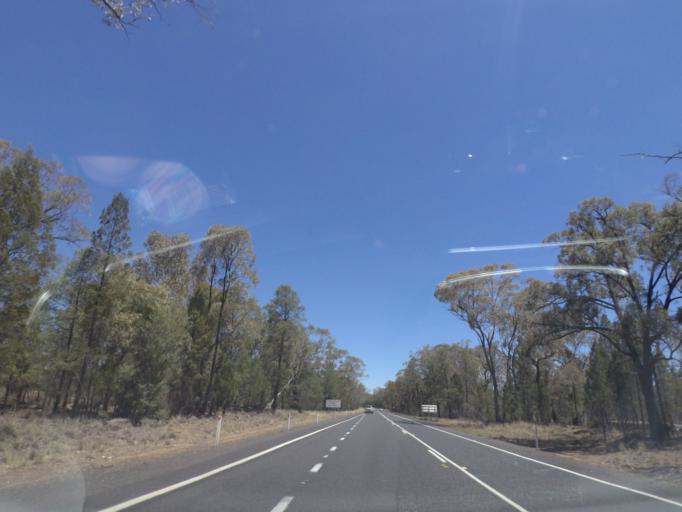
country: AU
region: New South Wales
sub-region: Warrumbungle Shire
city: Coonabarabran
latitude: -31.3416
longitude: 149.2972
